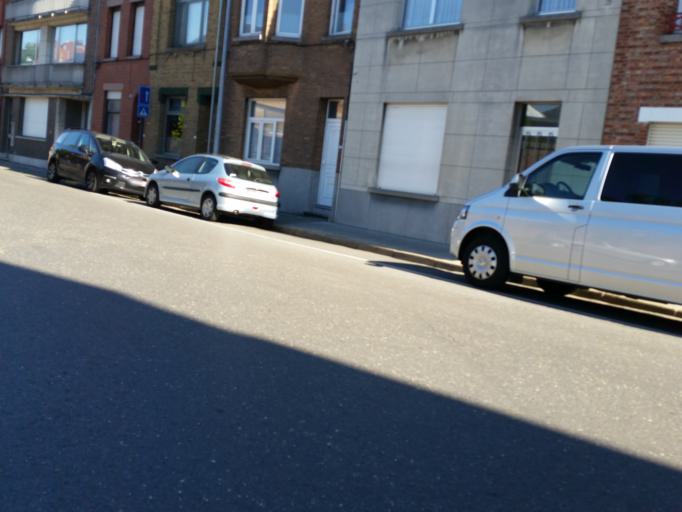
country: BE
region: Flanders
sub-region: Provincie Antwerpen
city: Mechelen
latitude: 51.0161
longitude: 4.4715
